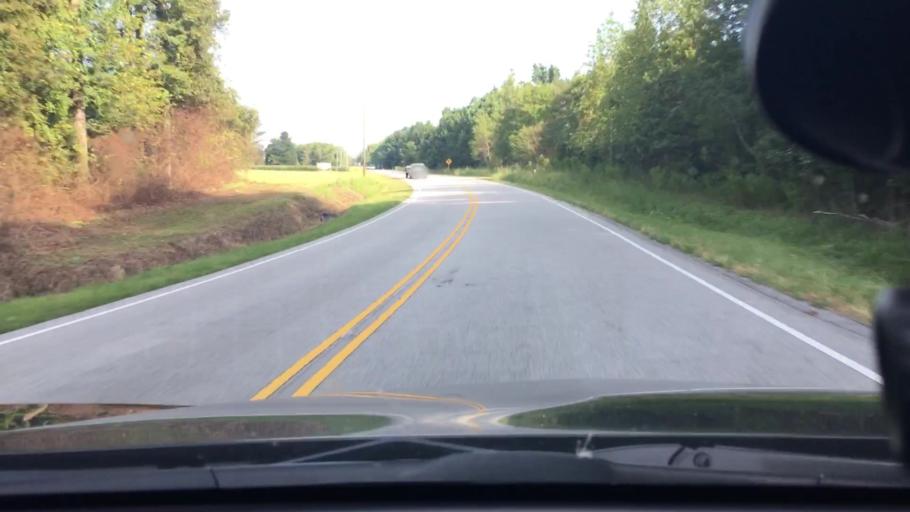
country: US
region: North Carolina
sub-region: Edgecombe County
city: Pinetops
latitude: 35.7341
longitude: -77.5333
